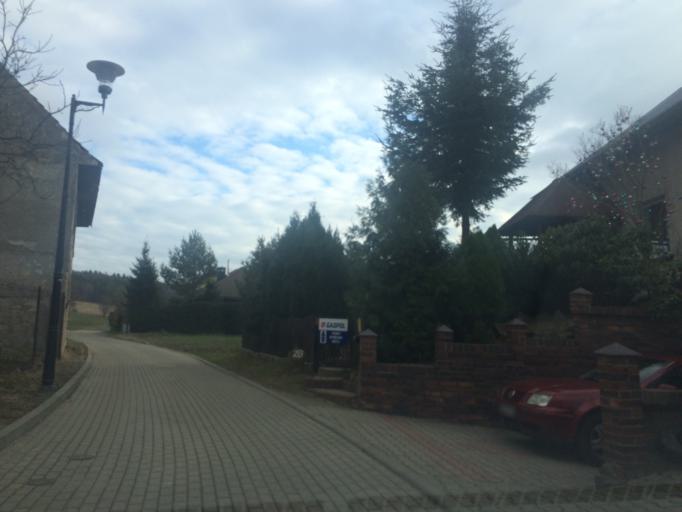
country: PL
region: Lower Silesian Voivodeship
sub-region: Powiat lwowecki
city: Lwowek Slaski
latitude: 51.1090
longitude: 15.6102
